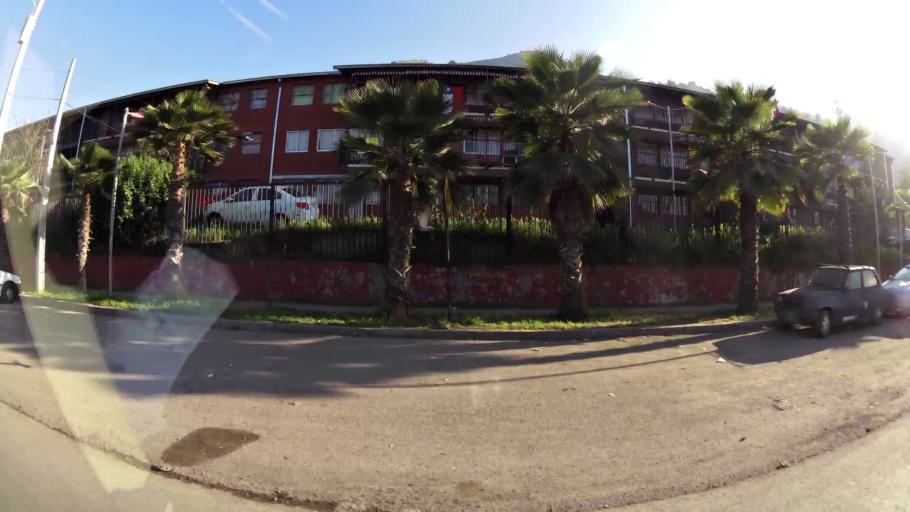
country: CL
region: Santiago Metropolitan
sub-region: Provincia de Santiago
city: Santiago
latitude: -33.3775
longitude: -70.6195
